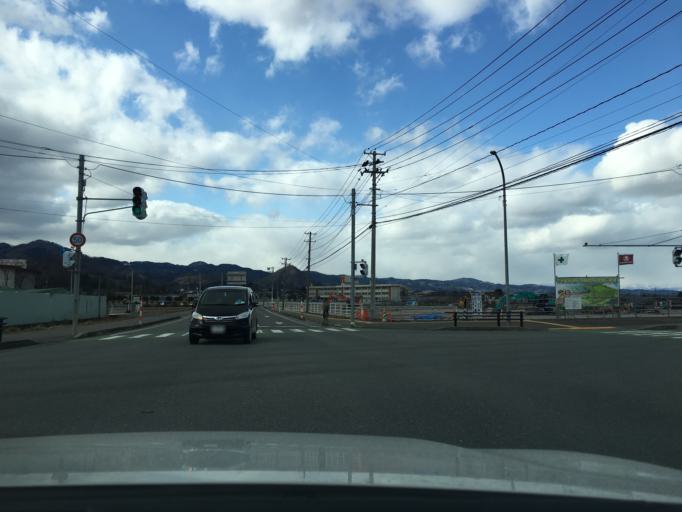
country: JP
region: Yamagata
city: Kaminoyama
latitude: 38.2096
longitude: 140.3001
